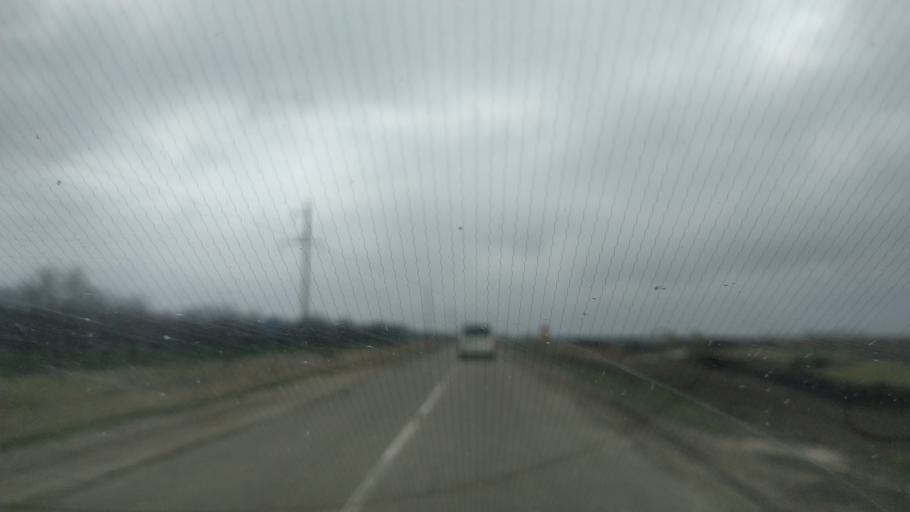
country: MD
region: Gagauzia
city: Bugeac
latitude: 46.3300
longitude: 28.7339
